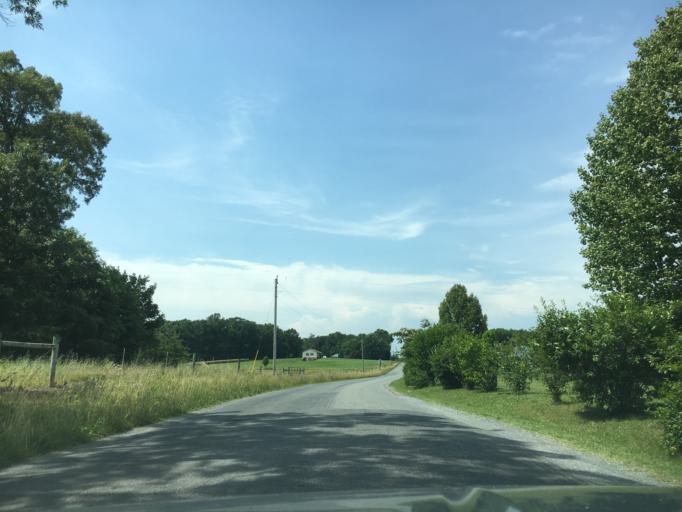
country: US
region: Virginia
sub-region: Pittsylvania County
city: Chatham
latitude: 36.8906
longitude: -79.4062
